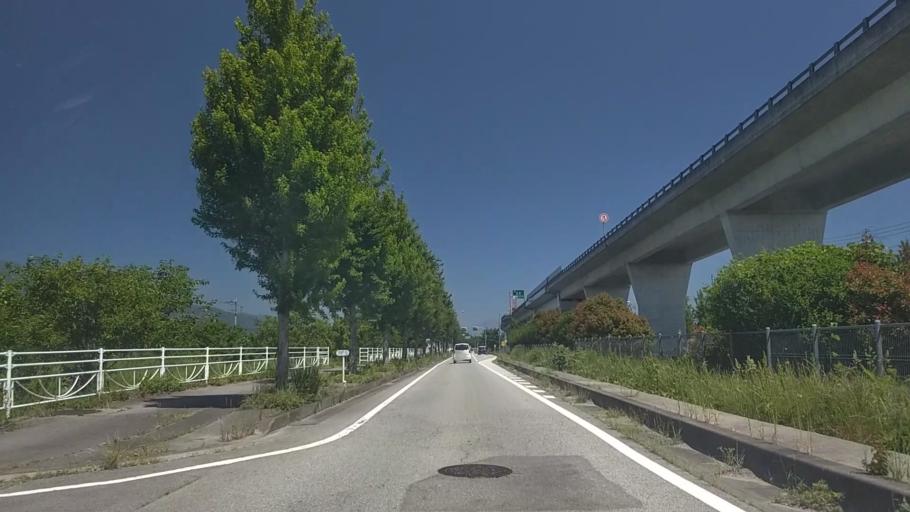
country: JP
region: Yamanashi
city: Ryuo
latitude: 35.6307
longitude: 138.4733
